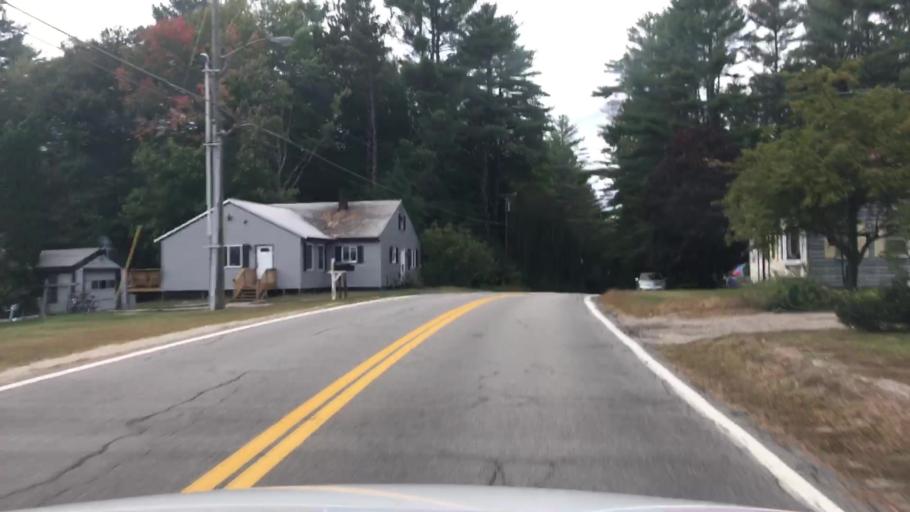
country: US
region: New Hampshire
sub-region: Carroll County
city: Effingham
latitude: 43.7237
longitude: -71.0000
